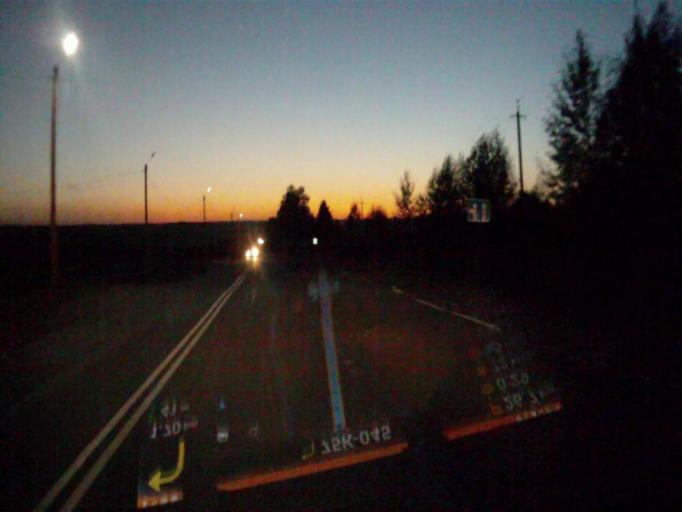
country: RU
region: Chelyabinsk
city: Chebarkul'
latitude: 55.2232
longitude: 60.4756
